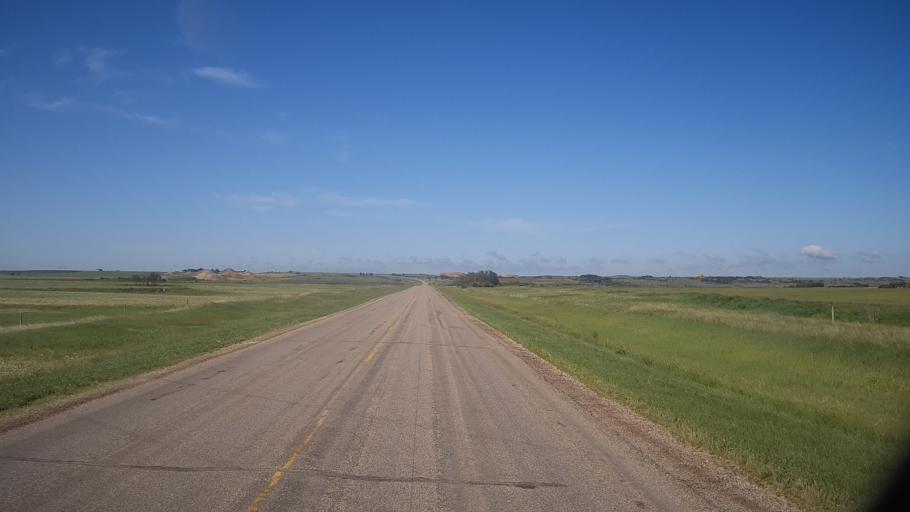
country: CA
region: Saskatchewan
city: Watrous
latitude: 51.7184
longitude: -105.3614
